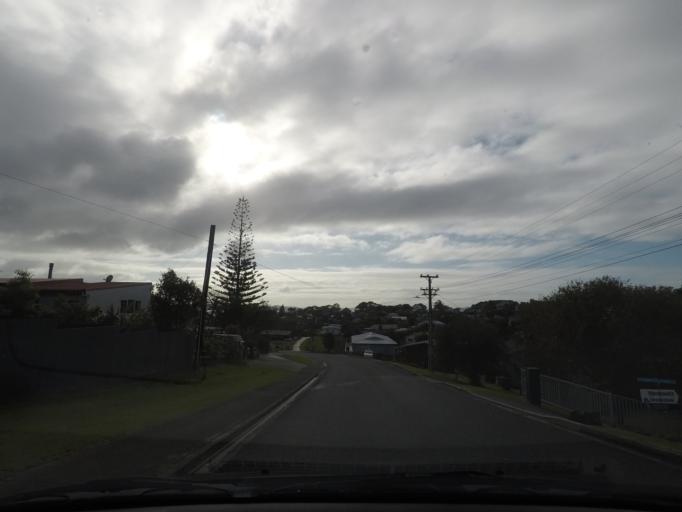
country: NZ
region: Auckland
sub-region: Auckland
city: Warkworth
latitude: -36.4279
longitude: 174.7348
